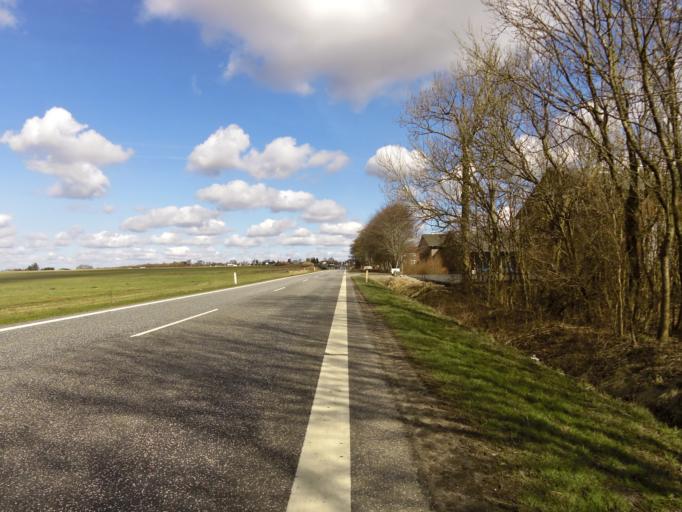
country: DK
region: South Denmark
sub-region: Tonder Kommune
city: Toftlund
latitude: 55.1746
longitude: 9.0574
